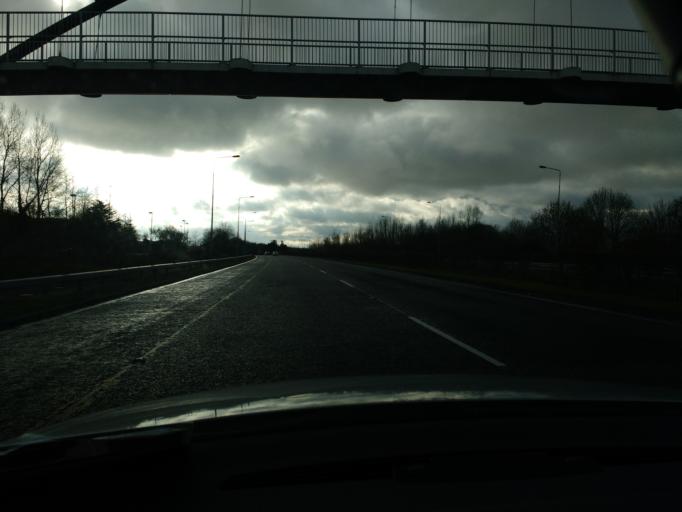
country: IE
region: Munster
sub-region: An Clar
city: Shannon
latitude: 52.7096
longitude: -8.8882
